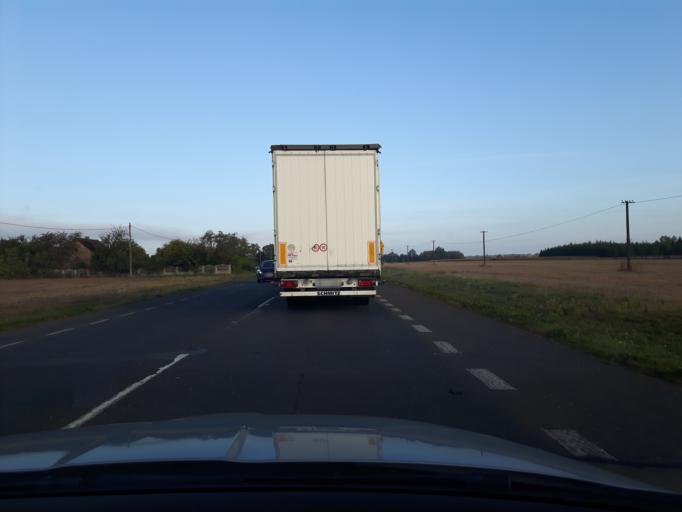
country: PL
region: Masovian Voivodeship
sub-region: Powiat plonski
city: Plonsk
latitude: 52.6834
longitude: 20.3621
